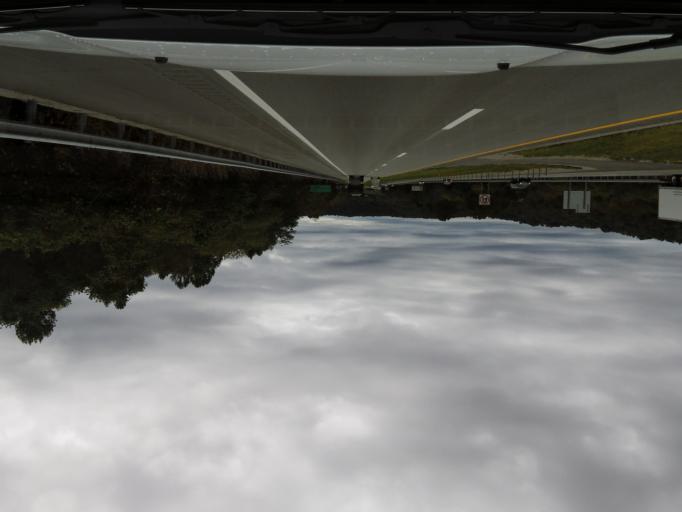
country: US
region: Kentucky
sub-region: Rockcastle County
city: Mount Vernon
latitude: 37.3492
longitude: -84.3078
